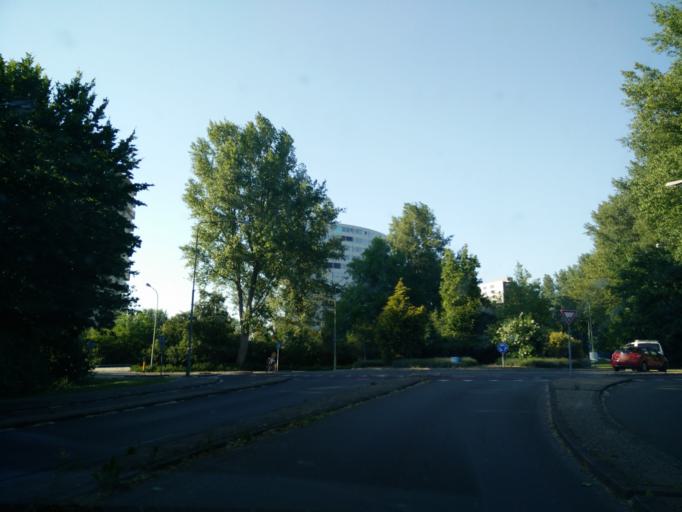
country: NL
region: South Holland
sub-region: Gemeente Dordrecht
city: Dordrecht
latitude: 51.7823
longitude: 4.6761
